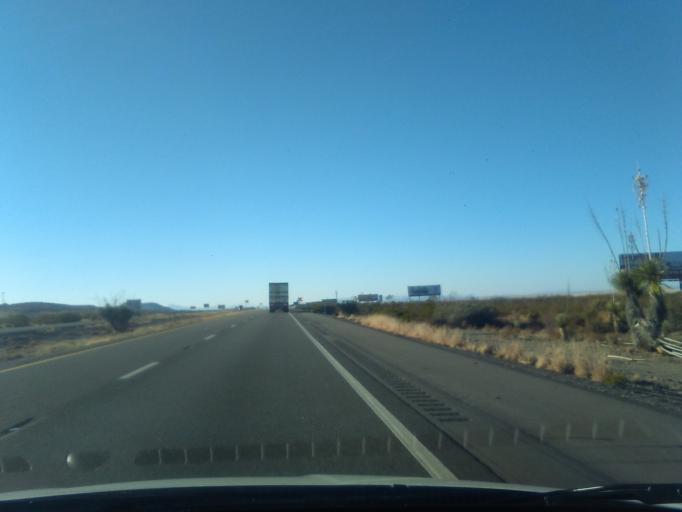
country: US
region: New Mexico
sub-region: Hidalgo County
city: Lordsburg
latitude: 32.3464
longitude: -108.7232
